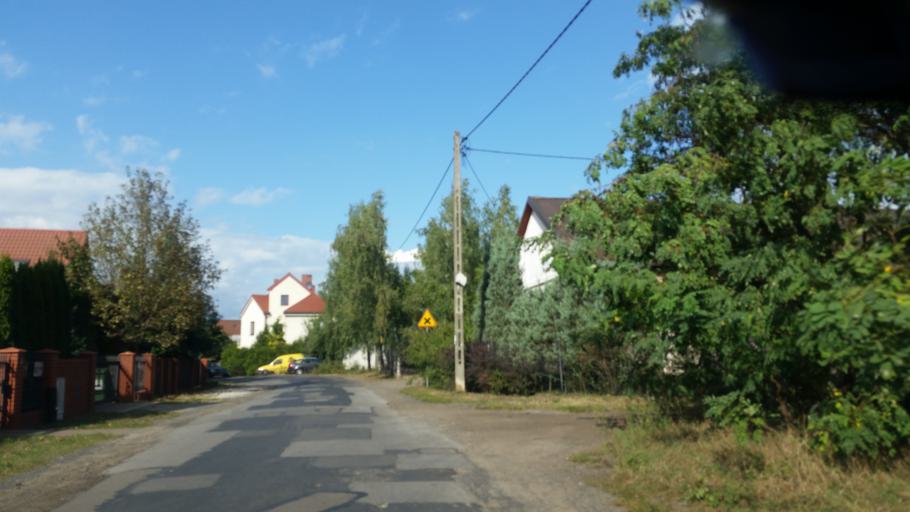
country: PL
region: Masovian Voivodeship
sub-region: Warszawa
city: Targowek
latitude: 52.3160
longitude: 21.0434
